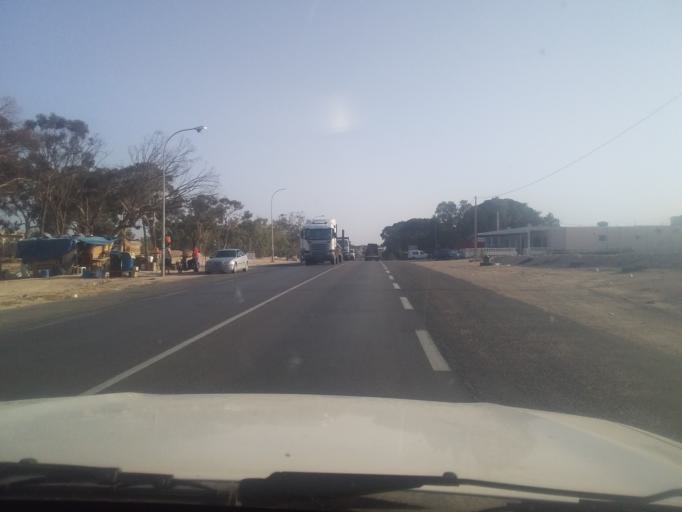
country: TN
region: Qabis
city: Gabes
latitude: 33.6337
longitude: 10.2820
